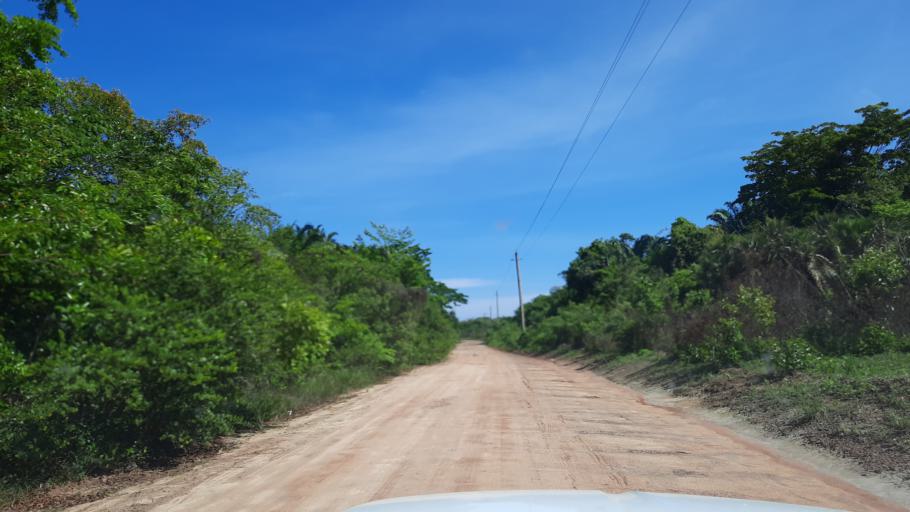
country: BZ
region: Stann Creek
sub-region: Dangriga
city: Dangriga
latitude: 17.1621
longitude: -88.3289
